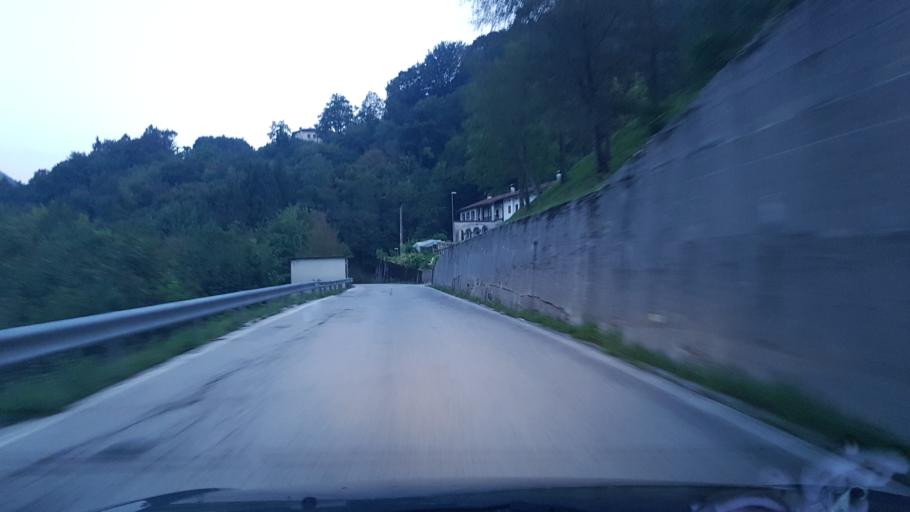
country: IT
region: Friuli Venezia Giulia
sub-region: Provincia di Pordenone
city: Frisanco
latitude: 46.2522
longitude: 12.7412
